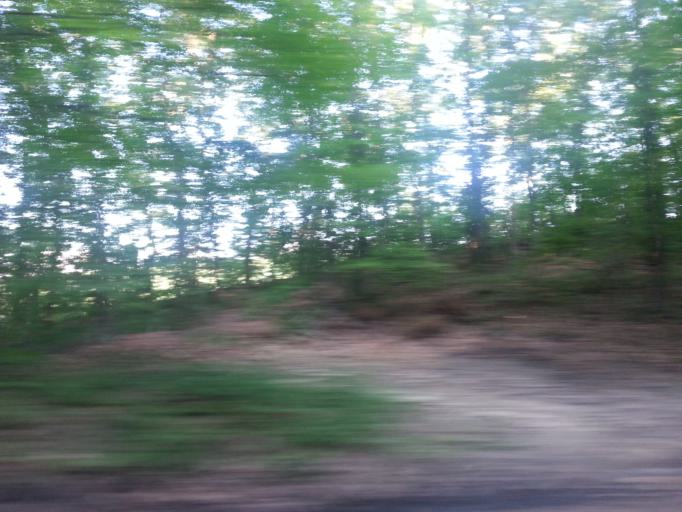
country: US
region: Tennessee
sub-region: Blount County
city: Maryville
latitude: 35.6670
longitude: -83.9060
